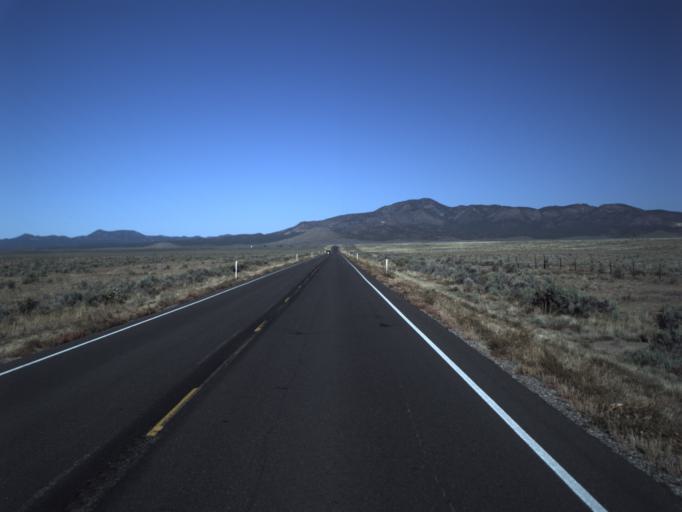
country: US
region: Utah
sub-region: Washington County
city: Enterprise
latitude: 37.7815
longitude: -113.8612
